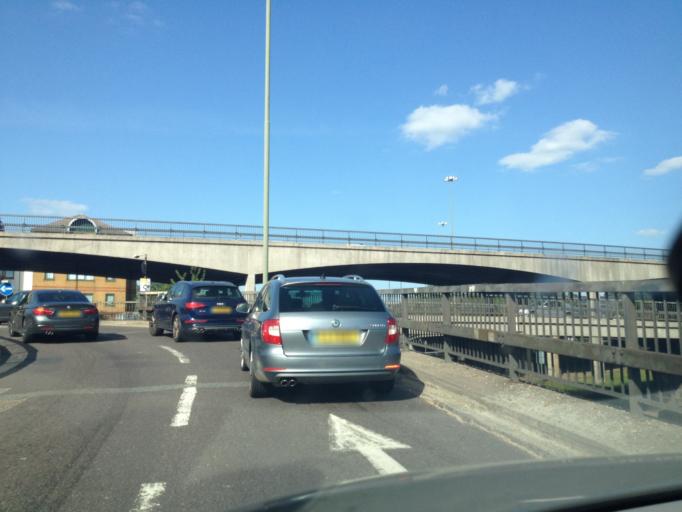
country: GB
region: England
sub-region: Greater London
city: Hendon
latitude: 51.5764
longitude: -0.2192
